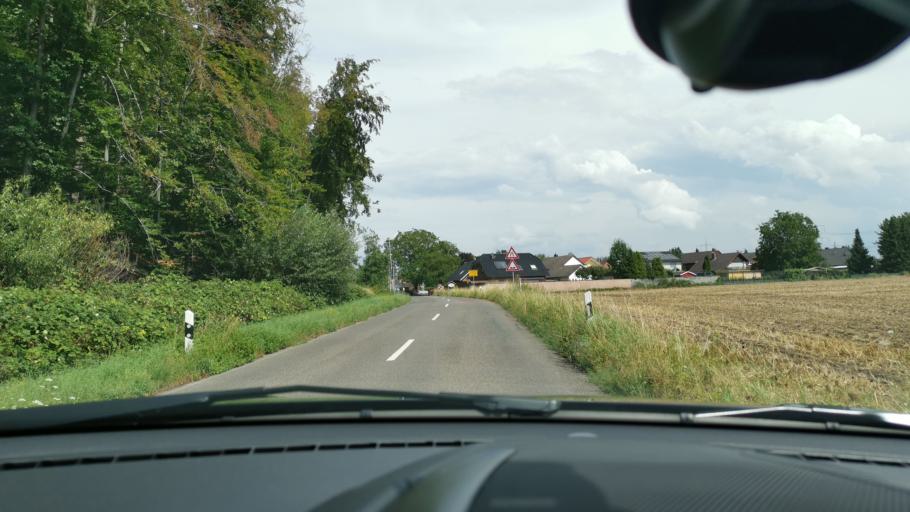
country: DE
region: North Rhine-Westphalia
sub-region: Regierungsbezirk Dusseldorf
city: Grevenbroich
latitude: 51.0579
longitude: 6.6212
